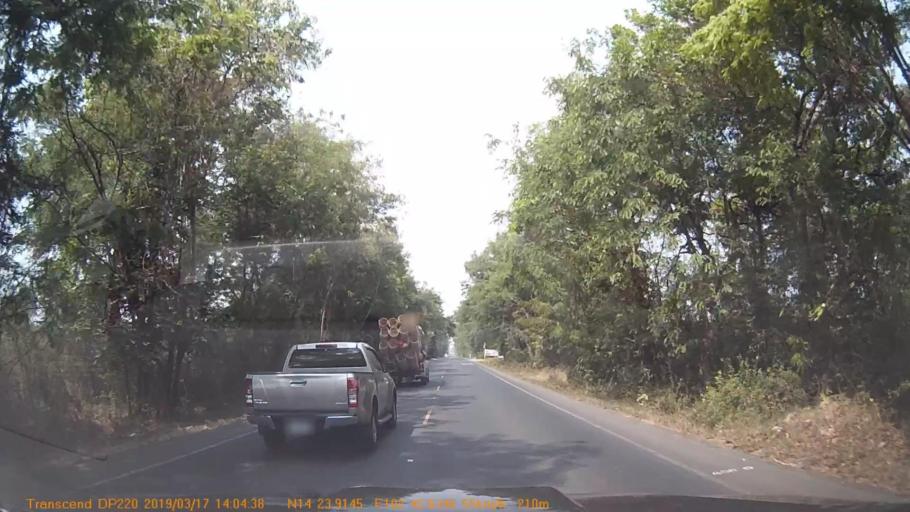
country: TH
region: Buriram
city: Pa Kham
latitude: 14.3989
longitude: 102.7107
